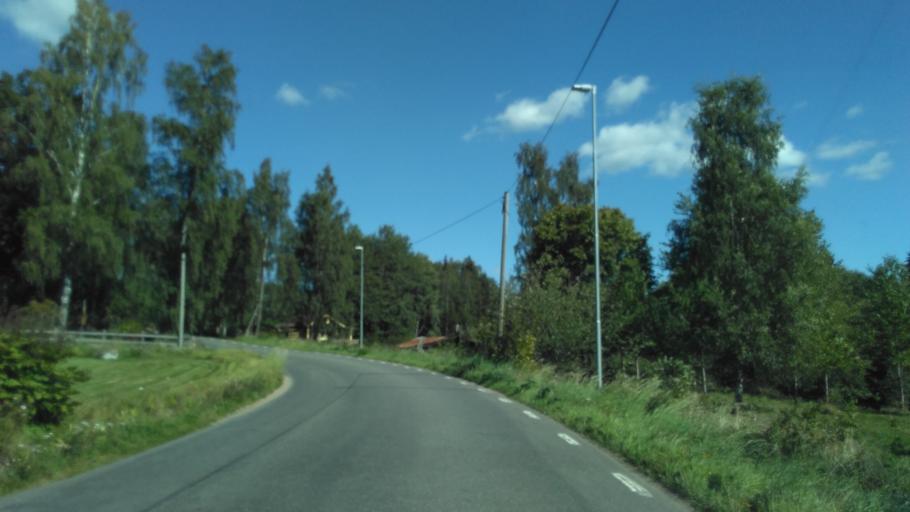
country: SE
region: Vaestra Goetaland
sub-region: Skara Kommun
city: Axvall
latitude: 58.4155
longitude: 13.6101
